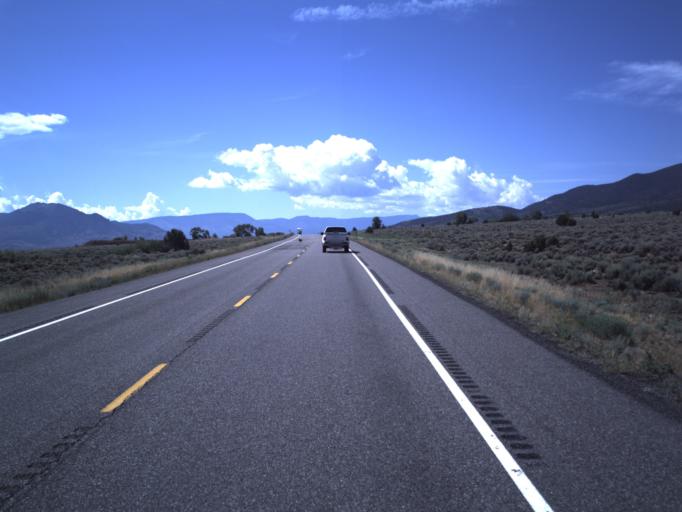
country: US
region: Utah
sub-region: Piute County
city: Junction
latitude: 38.3884
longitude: -112.2301
